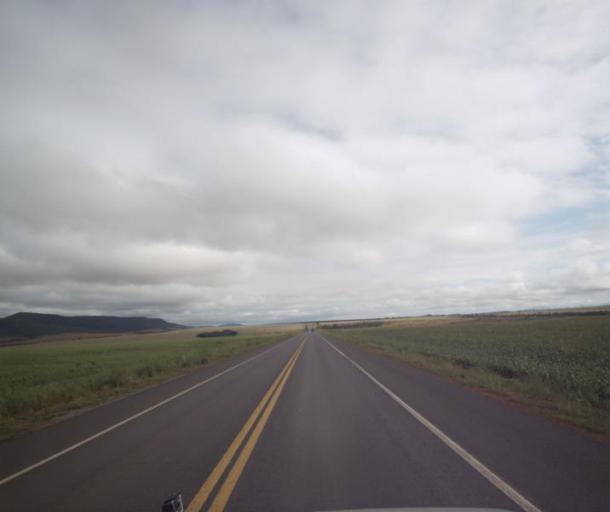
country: BR
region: Goias
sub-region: Padre Bernardo
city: Padre Bernardo
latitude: -15.4052
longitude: -48.6303
